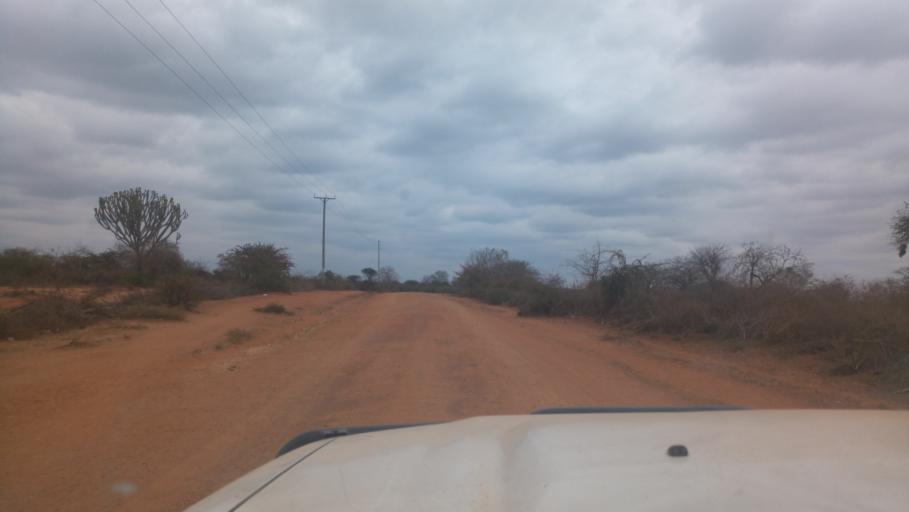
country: KE
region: Makueni
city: Makueni
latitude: -1.9507
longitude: 38.0565
